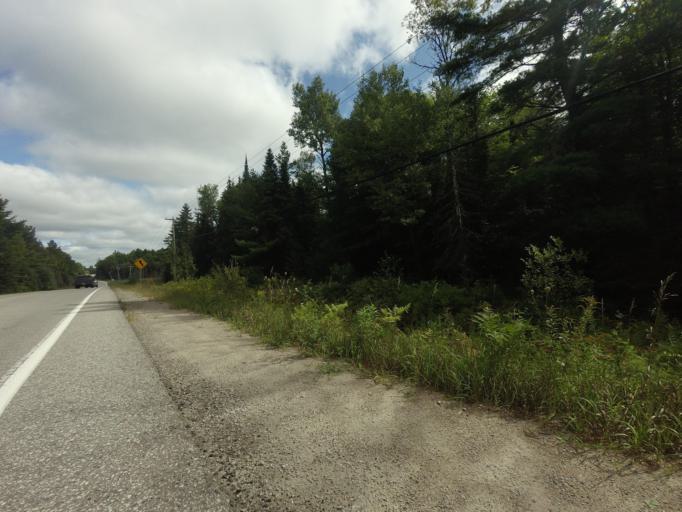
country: CA
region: Ontario
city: Omemee
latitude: 44.7885
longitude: -78.6438
